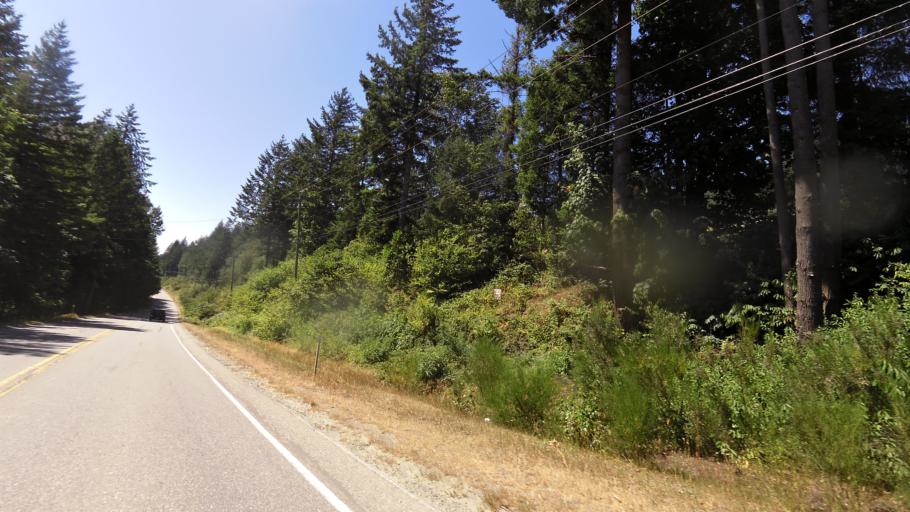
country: CA
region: British Columbia
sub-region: Fraser Valley Regional District
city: Chilliwack
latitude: 49.1997
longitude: -122.0467
